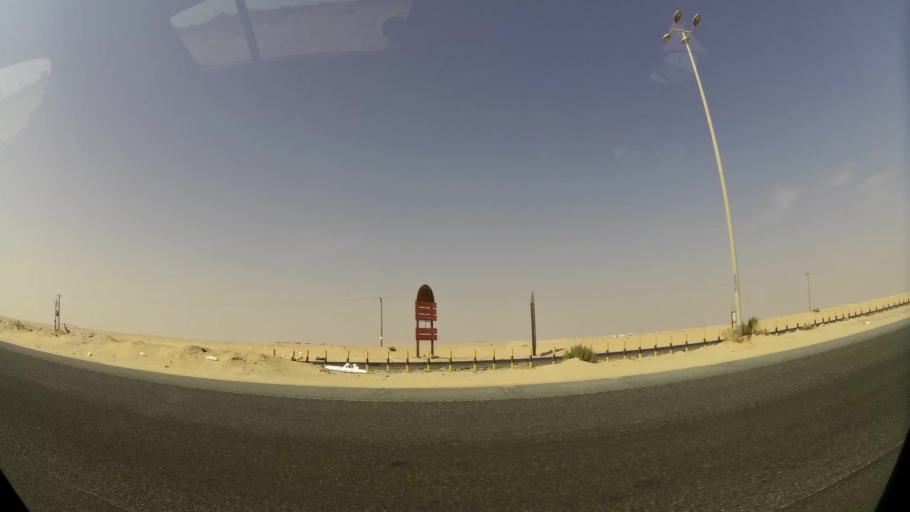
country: KW
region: Al Ahmadi
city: Al Wafrah
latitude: 28.8068
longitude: 48.0409
